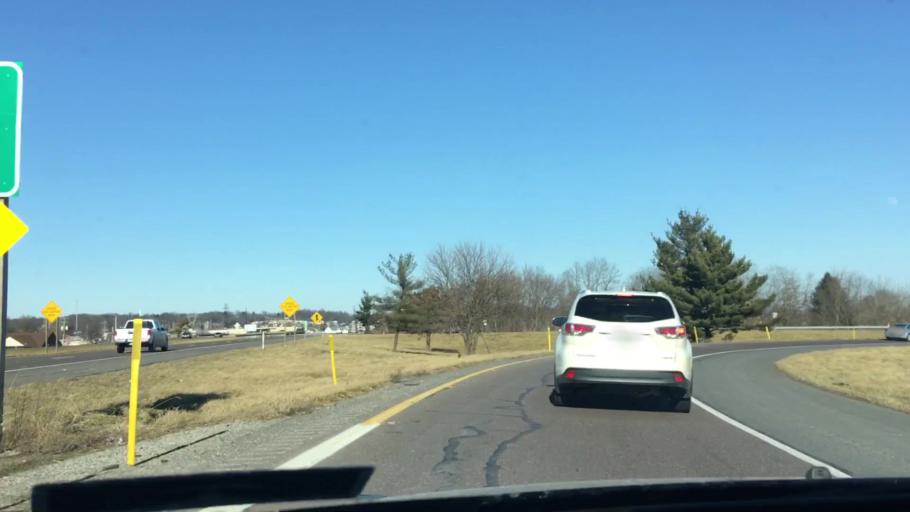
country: US
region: Pennsylvania
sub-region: Lancaster County
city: Brownstown
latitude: 40.1303
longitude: -76.2148
